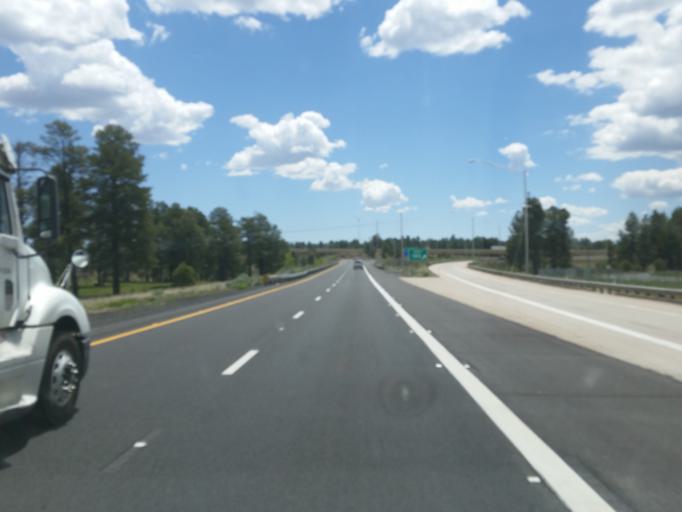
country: US
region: Arizona
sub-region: Coconino County
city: Flagstaff
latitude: 35.1739
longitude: -111.6686
